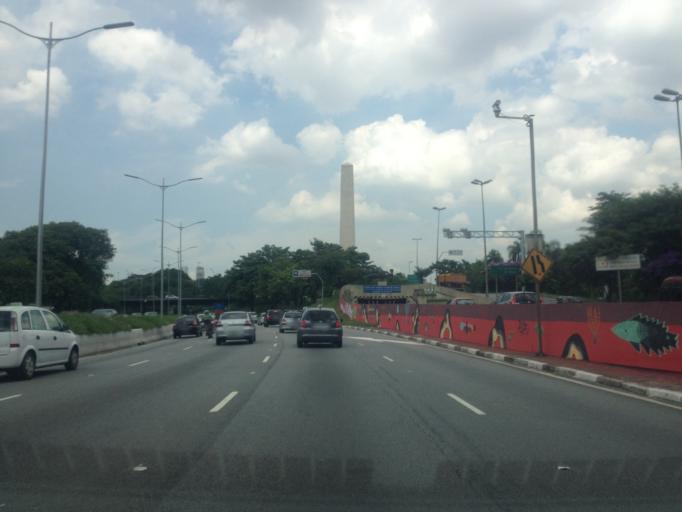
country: BR
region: Sao Paulo
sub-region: Sao Paulo
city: Sao Paulo
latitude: -23.5828
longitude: -46.6522
